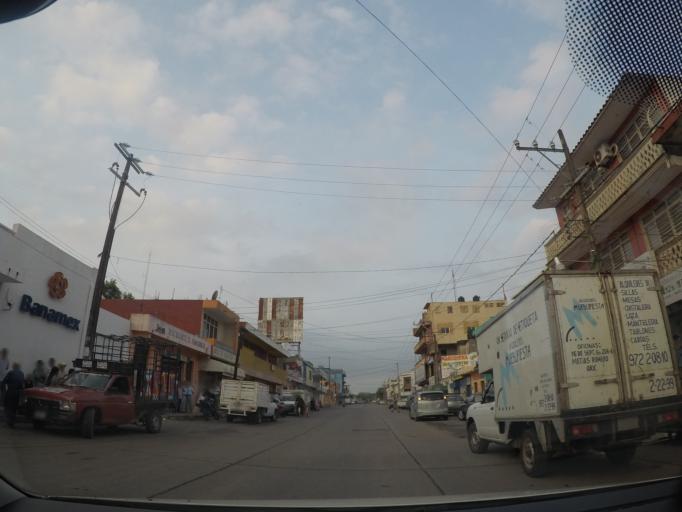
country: MX
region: Oaxaca
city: Matias Romero
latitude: 16.8786
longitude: -95.0425
